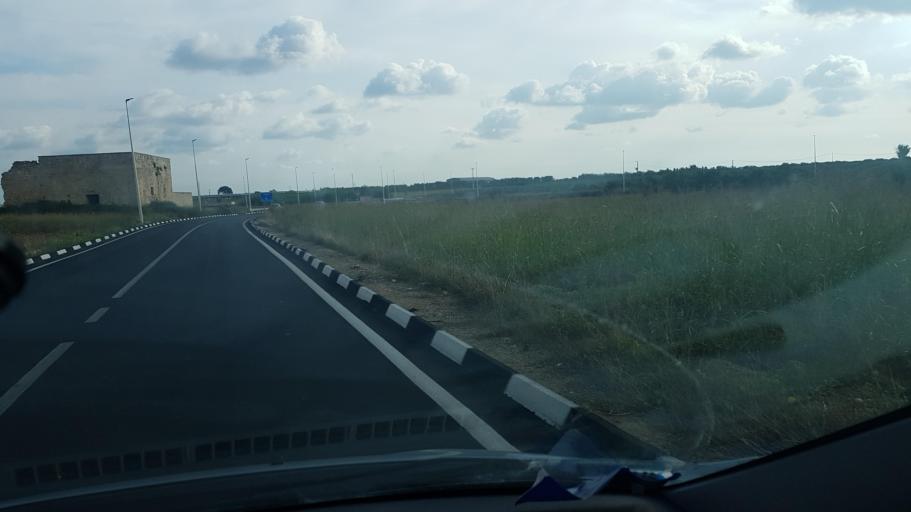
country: IT
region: Apulia
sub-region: Provincia di Brindisi
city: Cellino San Marco
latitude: 40.4407
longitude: 17.9551
